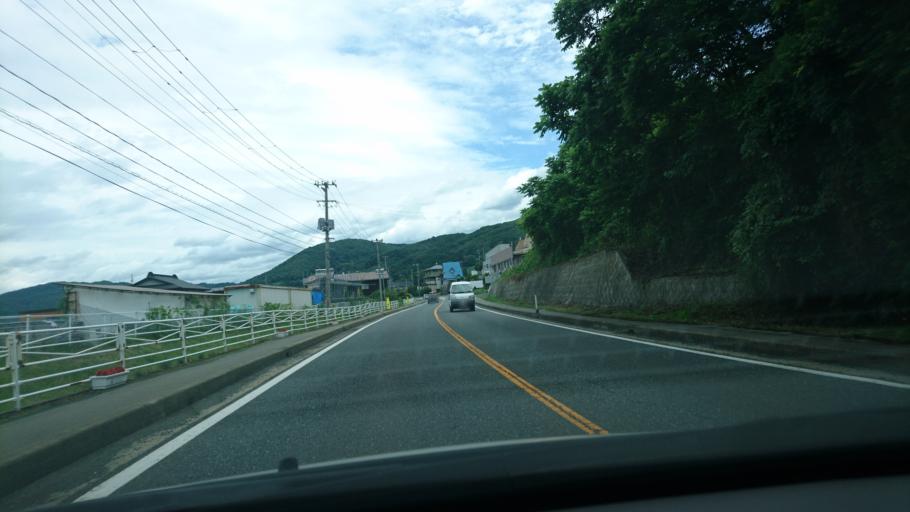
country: JP
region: Iwate
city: Morioka-shi
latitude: 39.6356
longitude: 141.1848
